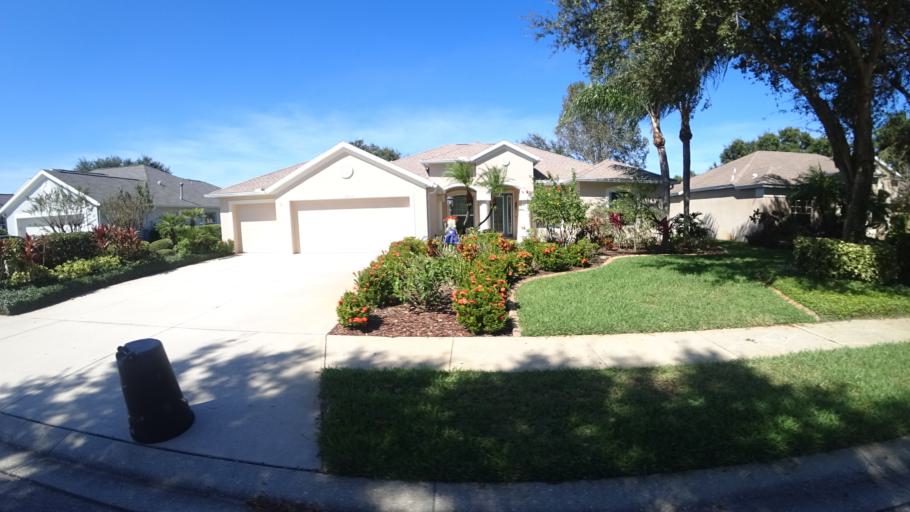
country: US
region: Florida
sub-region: Sarasota County
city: The Meadows
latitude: 27.4245
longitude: -82.4224
